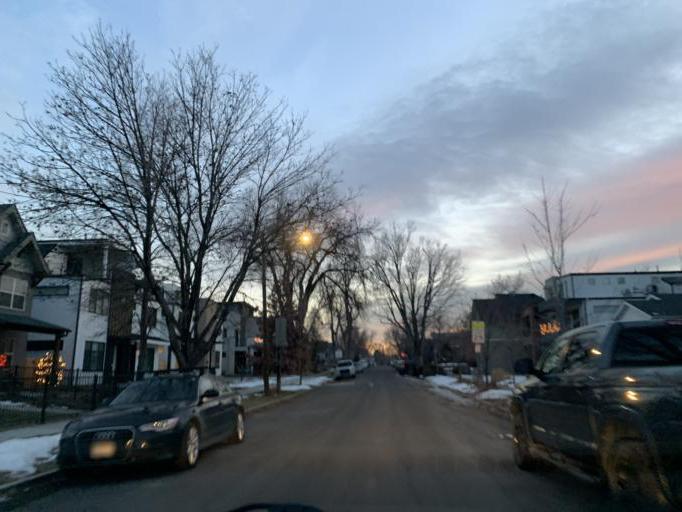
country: US
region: Colorado
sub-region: Adams County
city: Berkley
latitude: 39.7796
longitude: -105.0428
